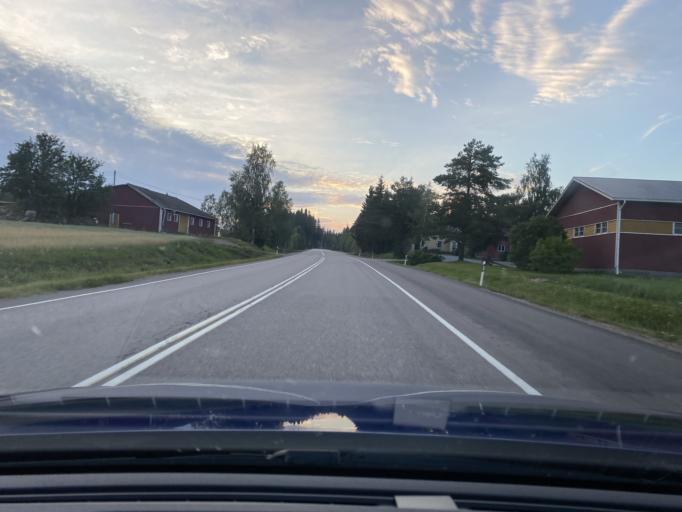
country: FI
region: Satakunta
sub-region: Pohjois-Satakunta
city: Kankaanpaeae
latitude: 61.8566
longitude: 22.3250
